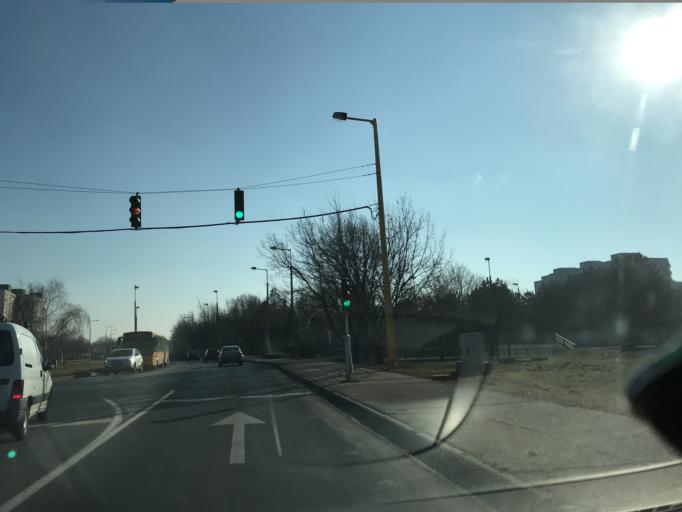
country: HU
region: Gyor-Moson-Sopron
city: Gyor
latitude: 47.6673
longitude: 17.6355
